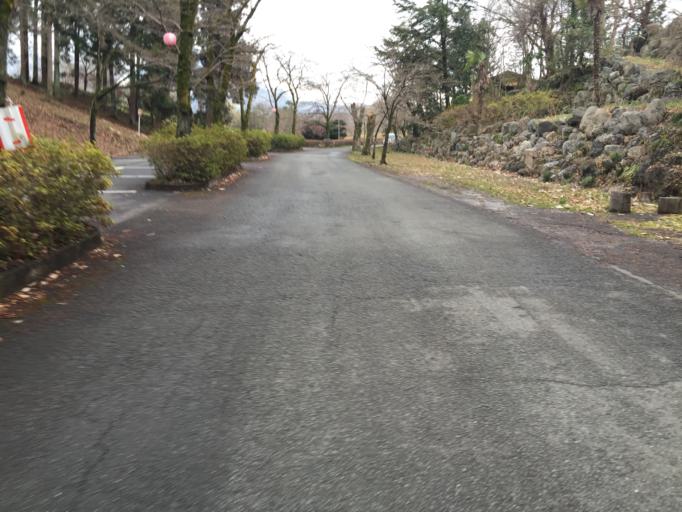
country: JP
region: Saitama
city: Chichibu
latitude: 35.9855
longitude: 139.0882
